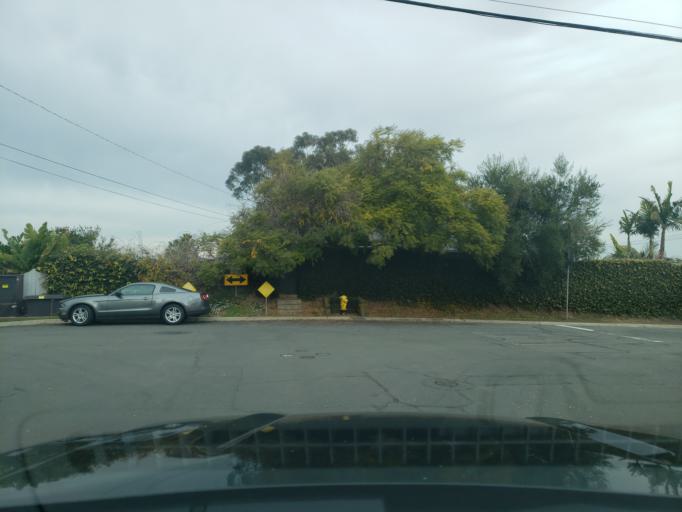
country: US
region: California
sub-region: San Diego County
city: Coronado
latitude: 32.7194
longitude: -117.2432
